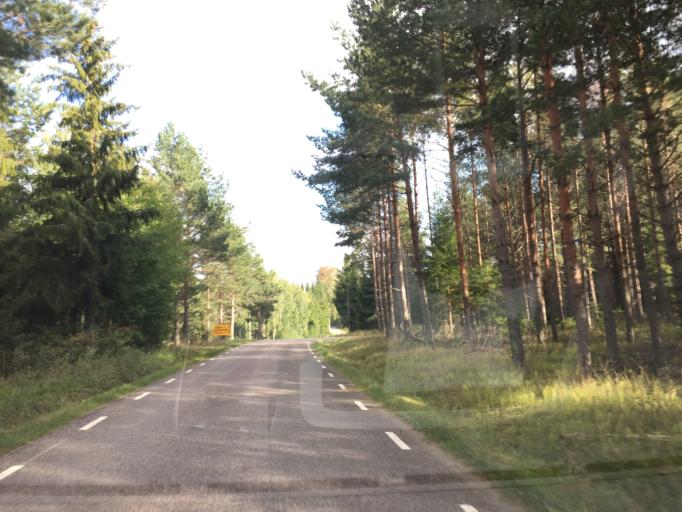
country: SE
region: Soedermanland
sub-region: Vingakers Kommun
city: Vingaker
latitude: 59.0066
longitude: 15.7592
